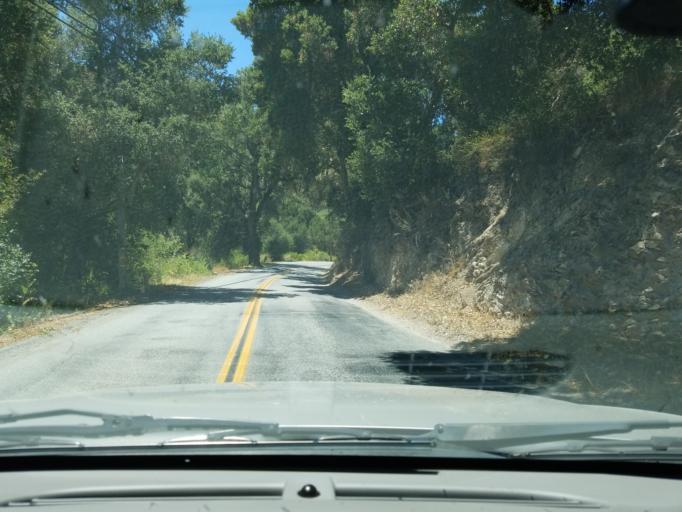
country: US
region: California
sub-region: Monterey County
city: Carmel Valley Village
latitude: 36.4548
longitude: -121.7005
